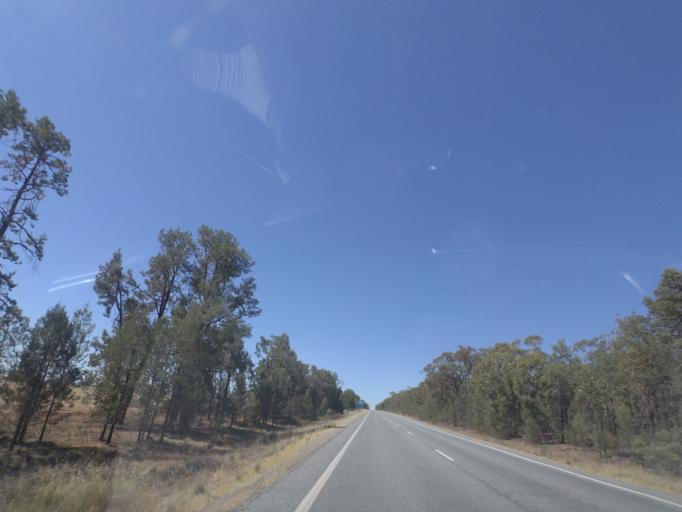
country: AU
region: New South Wales
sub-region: Narrandera
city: Narrandera
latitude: -34.4291
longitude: 146.8435
